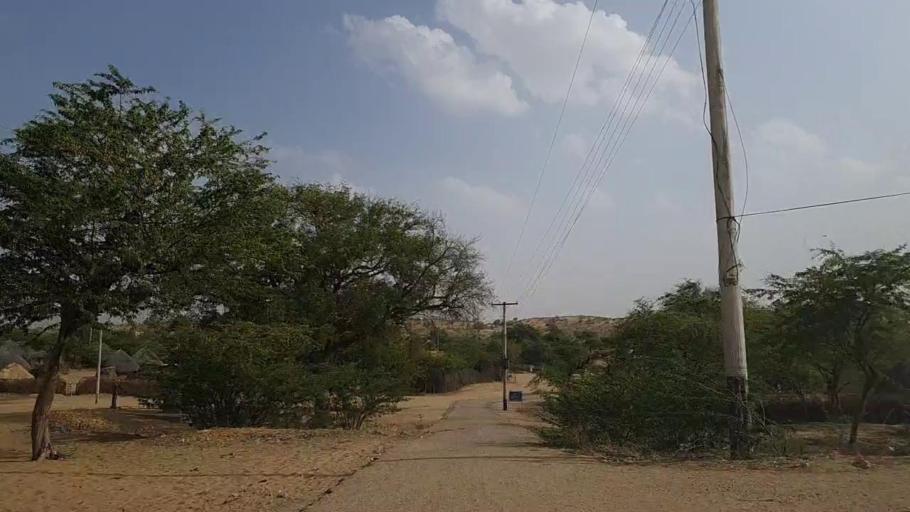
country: PK
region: Sindh
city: Islamkot
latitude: 24.8708
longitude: 70.1662
